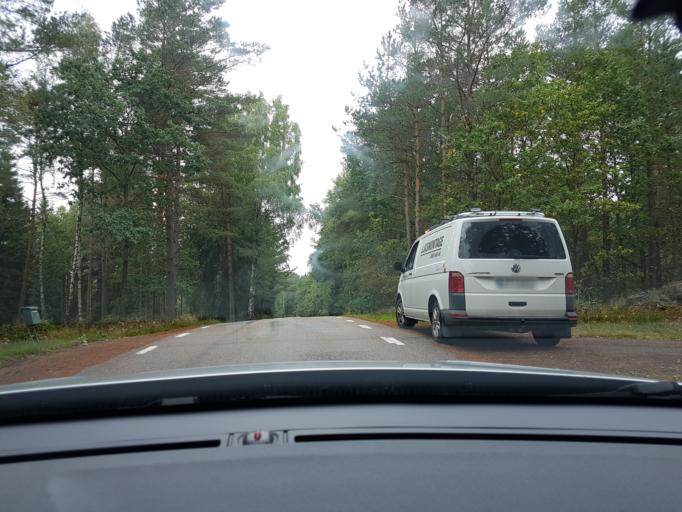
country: SE
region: Vaestra Goetaland
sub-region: Ale Kommun
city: Alvangen
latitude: 57.9040
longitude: 12.1772
